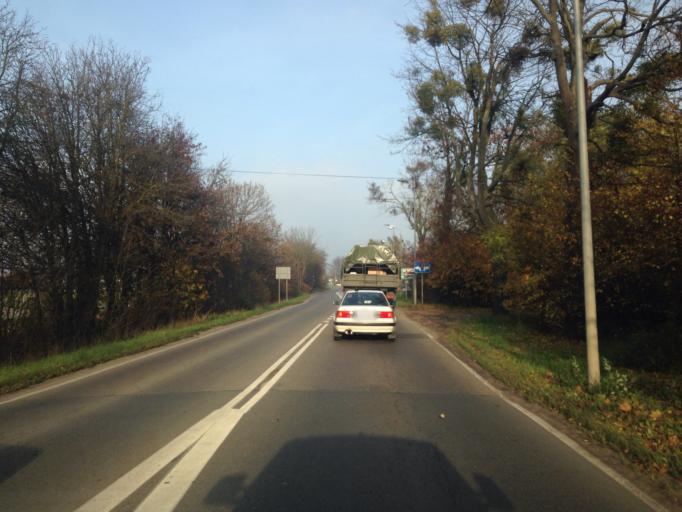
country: PL
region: Kujawsko-Pomorskie
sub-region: Powiat bydgoski
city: Osielsko
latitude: 53.1709
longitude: 18.0504
